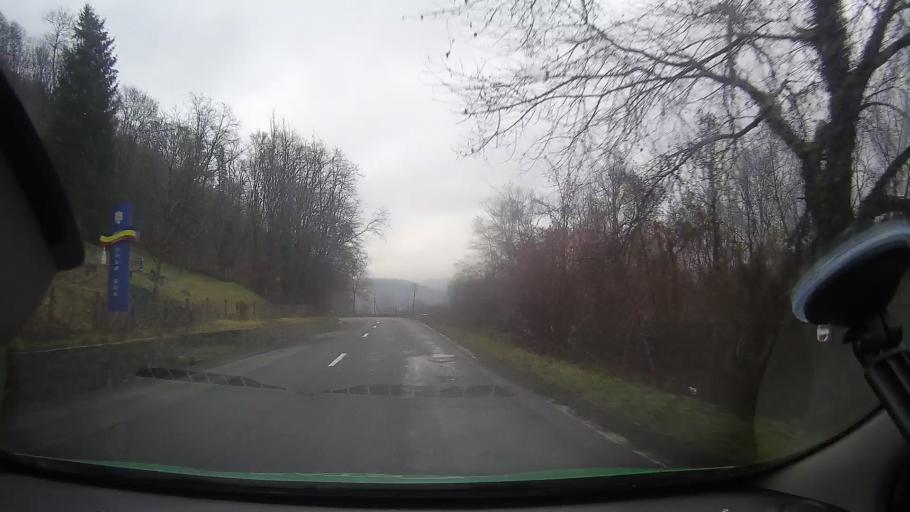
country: RO
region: Arad
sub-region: Comuna Gurahont
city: Gurahont
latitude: 46.2752
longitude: 22.3743
